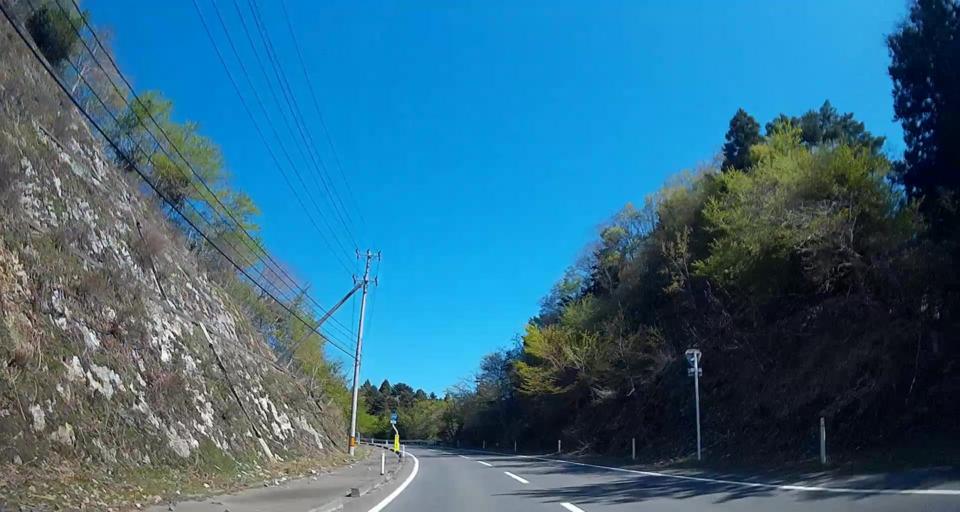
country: JP
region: Miyagi
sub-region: Oshika Gun
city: Onagawa Cho
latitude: 38.5063
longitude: 141.4867
